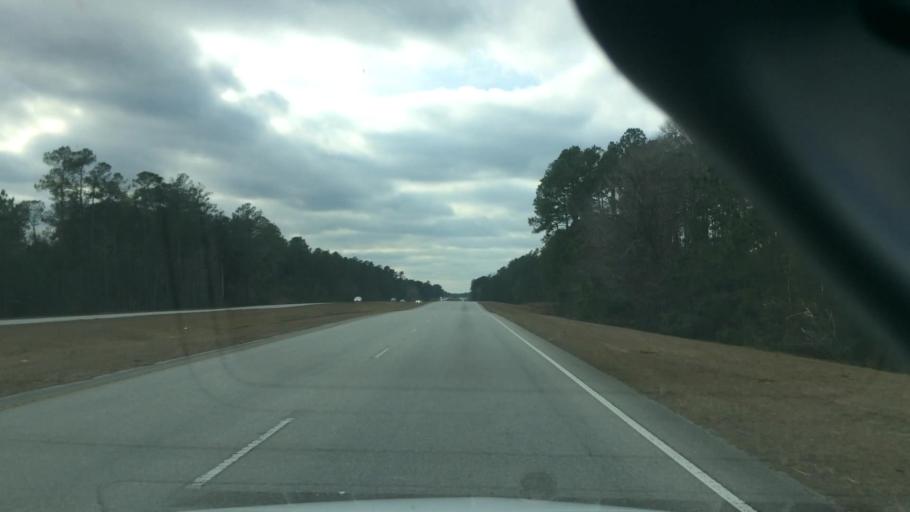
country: US
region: North Carolina
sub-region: Brunswick County
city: Bolivia
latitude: 34.0486
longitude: -78.2241
